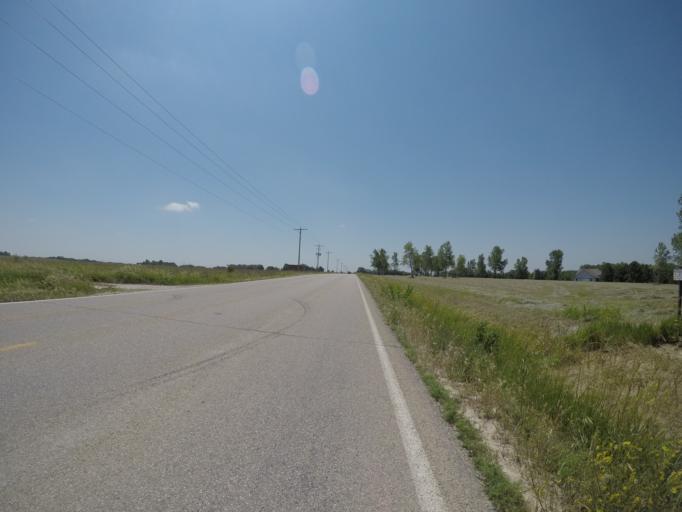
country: US
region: Kansas
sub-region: Riley County
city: Manhattan
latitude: 39.2253
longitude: -96.4407
